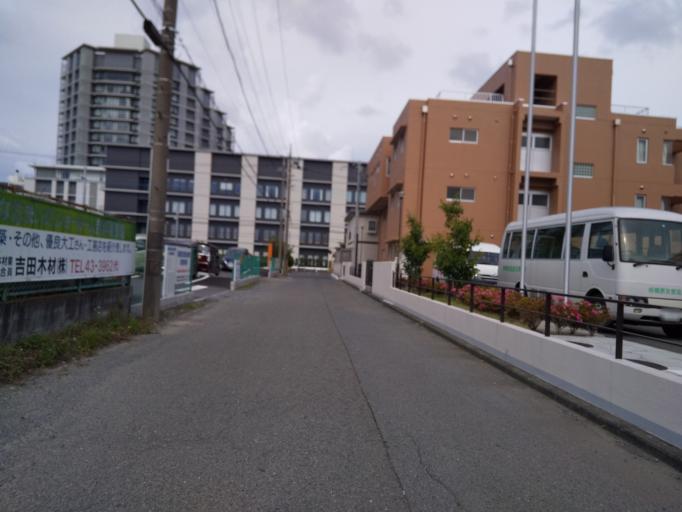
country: JP
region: Kanagawa
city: Zama
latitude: 35.5376
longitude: 139.3908
